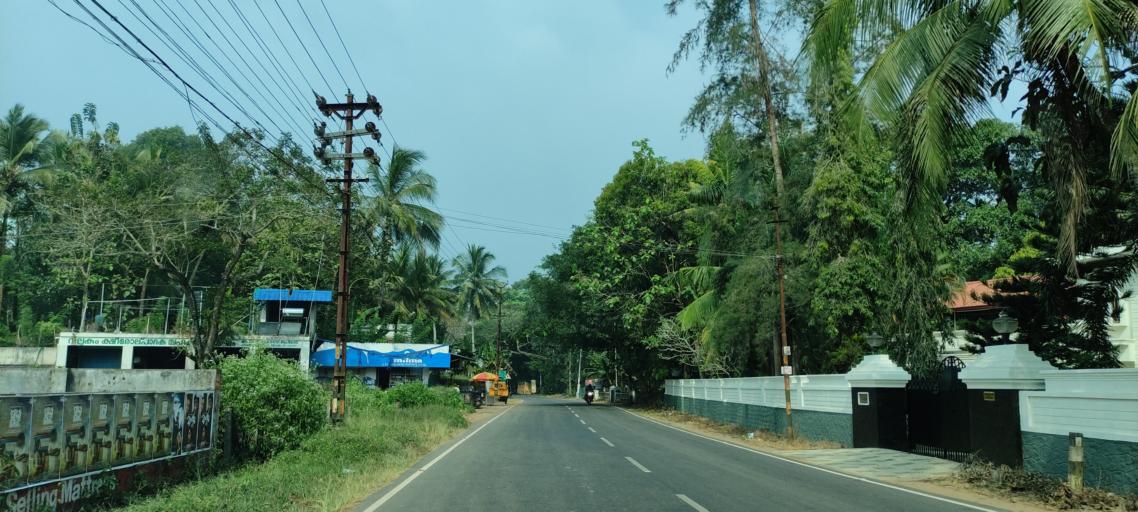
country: IN
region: Kerala
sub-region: Kottayam
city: Vaikam
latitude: 9.7683
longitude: 76.4177
